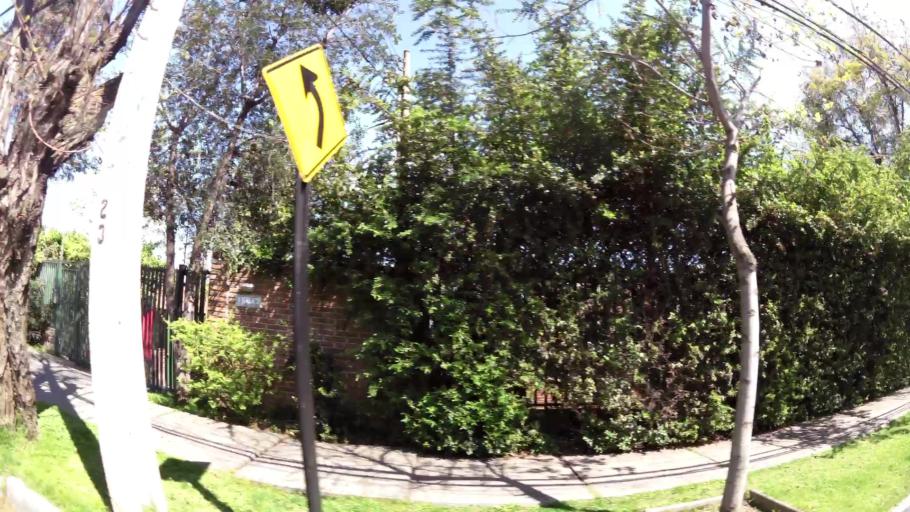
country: CL
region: Santiago Metropolitan
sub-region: Provincia de Santiago
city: Villa Presidente Frei, Nunoa, Santiago, Chile
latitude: -33.4445
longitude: -70.5236
